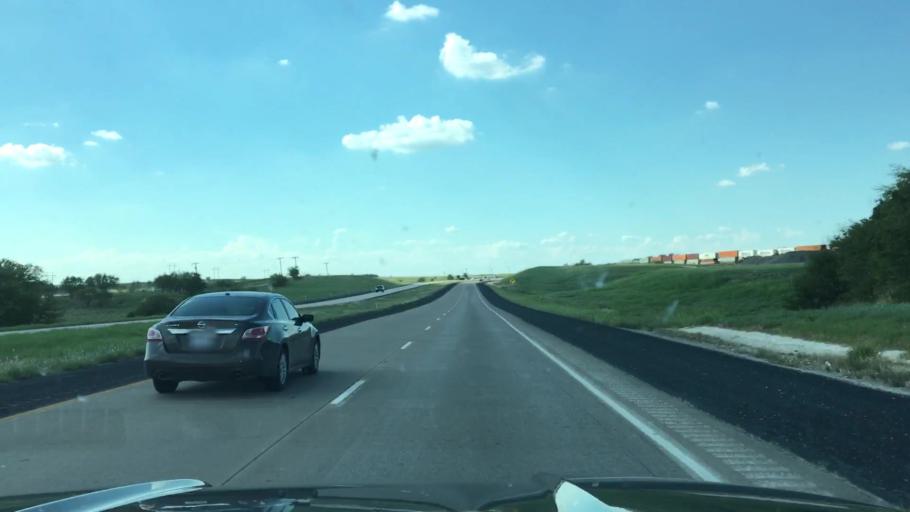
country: US
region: Texas
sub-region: Wise County
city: New Fairview
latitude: 33.1218
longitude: -97.4854
